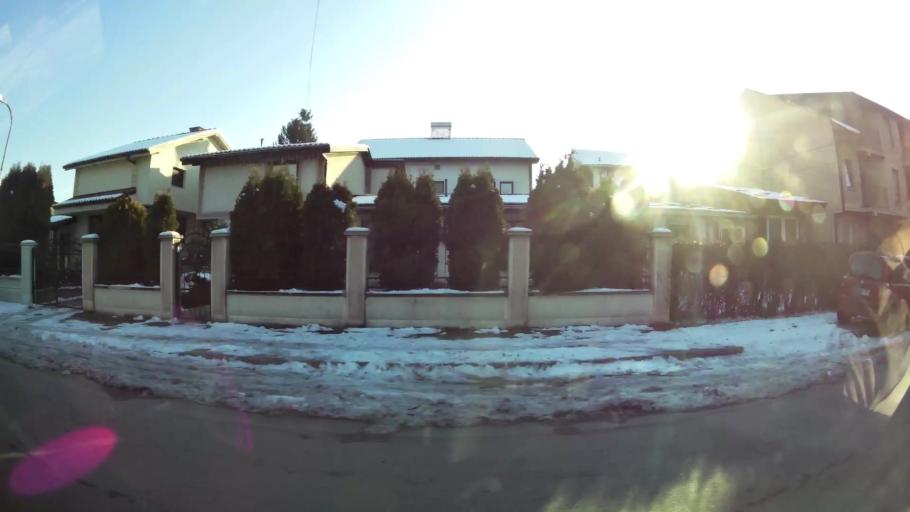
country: MK
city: Krushopek
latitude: 42.0013
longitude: 21.3857
